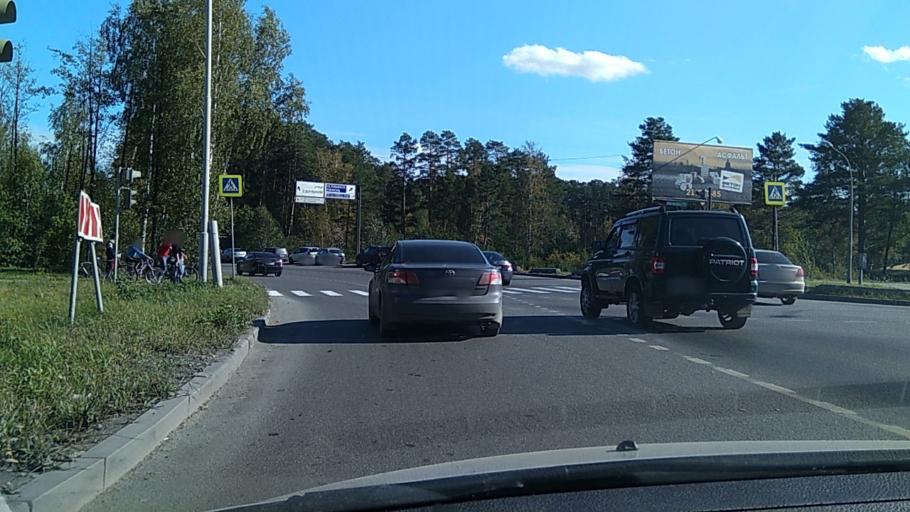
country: RU
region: Sverdlovsk
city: Sovkhoznyy
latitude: 56.8035
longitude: 60.5380
